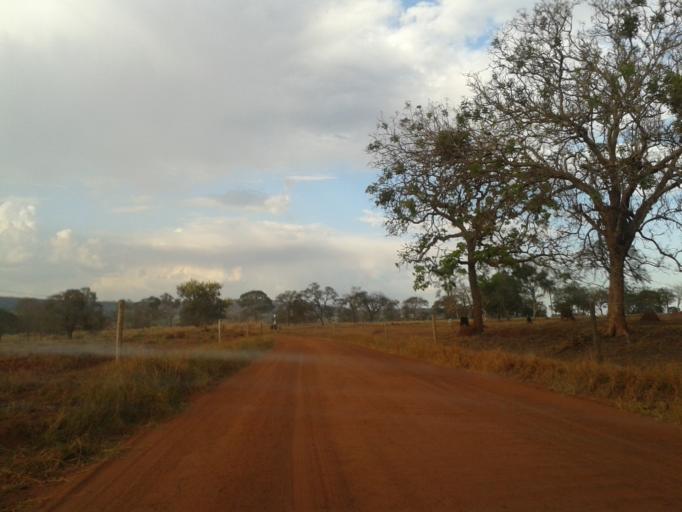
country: BR
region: Minas Gerais
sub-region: Ituiutaba
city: Ituiutaba
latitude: -19.1991
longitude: -49.8373
